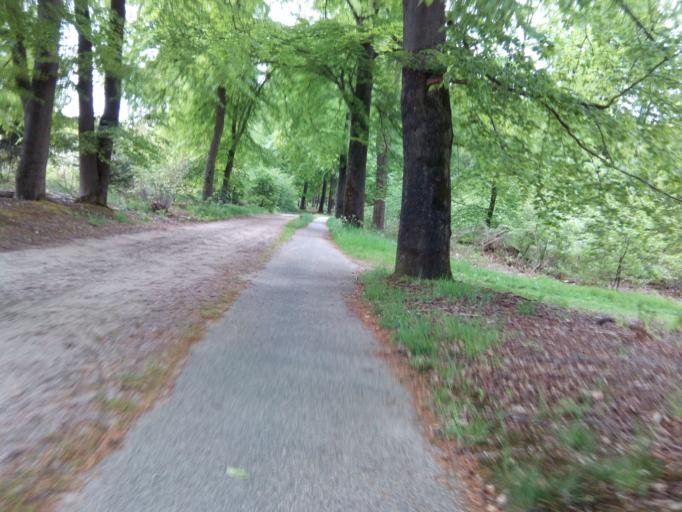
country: NL
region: Gelderland
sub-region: Gemeente Renkum
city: Wolfheze
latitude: 52.0170
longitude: 5.7693
